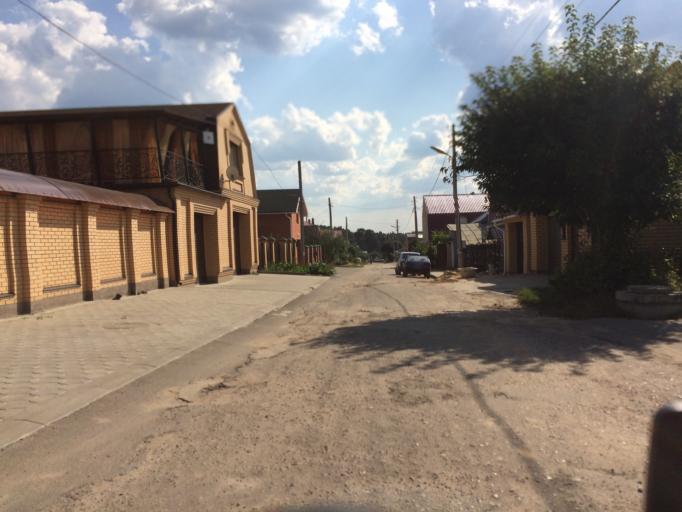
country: RU
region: Mariy-El
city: Yoshkar-Ola
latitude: 56.6209
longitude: 47.9483
